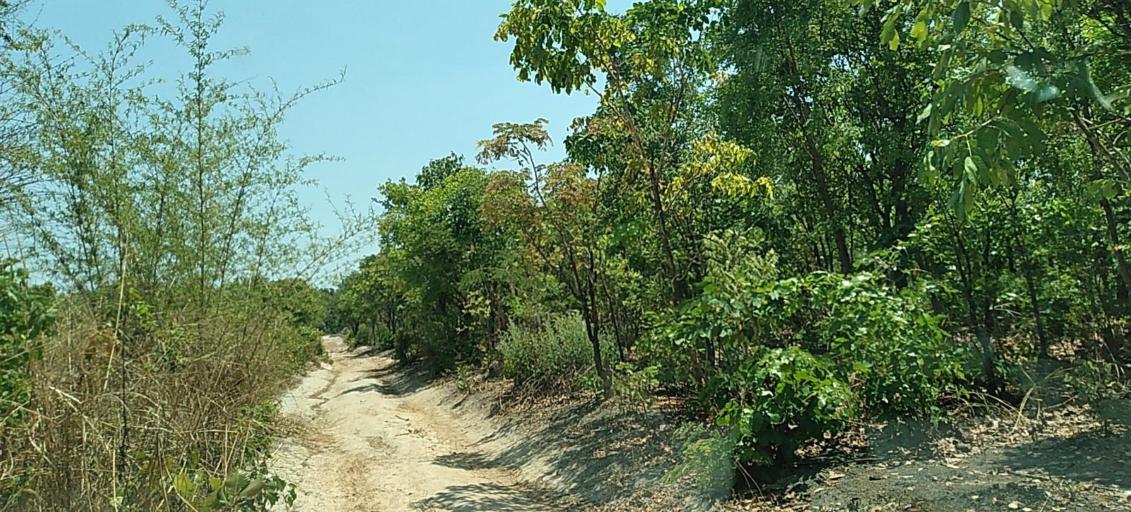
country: ZM
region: Copperbelt
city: Luanshya
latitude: -12.9854
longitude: 28.3290
